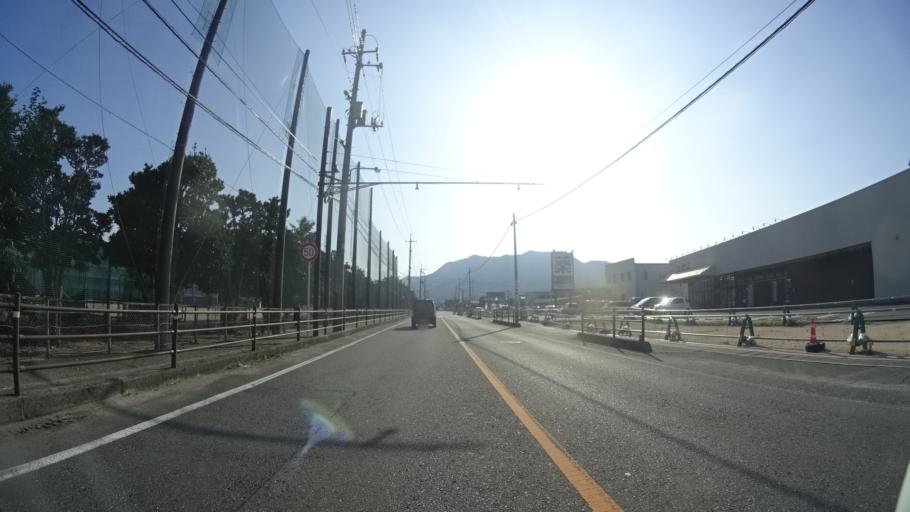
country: JP
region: Yamaguchi
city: Hagi
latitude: 34.4085
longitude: 131.3939
